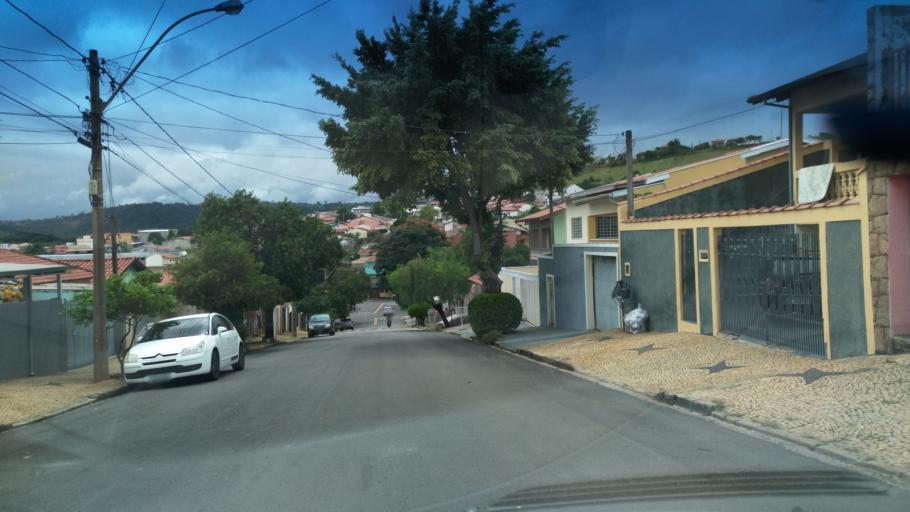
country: BR
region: Sao Paulo
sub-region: Valinhos
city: Valinhos
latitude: -22.9520
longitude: -46.9771
